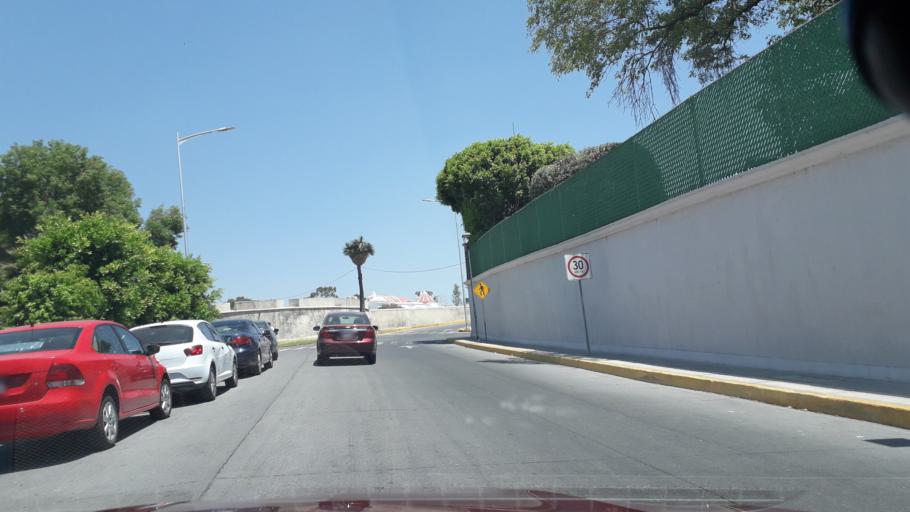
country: MX
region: Puebla
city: Puebla
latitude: 19.0564
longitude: -98.1865
